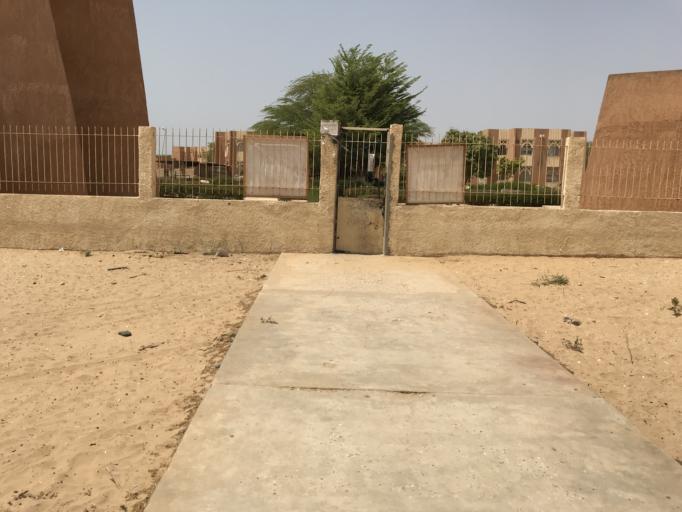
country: SN
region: Saint-Louis
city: Saint-Louis
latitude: 16.0631
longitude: -16.4255
